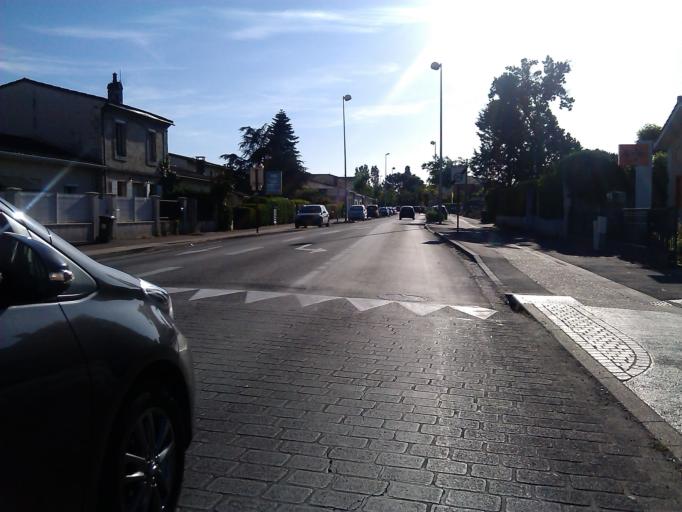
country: FR
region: Aquitaine
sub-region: Departement de la Gironde
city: Pessac
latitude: 44.8025
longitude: -0.6493
